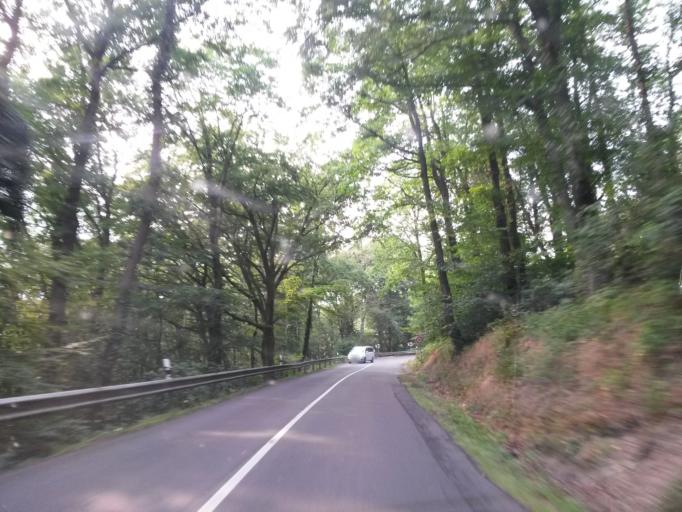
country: DE
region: North Rhine-Westphalia
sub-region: Regierungsbezirk Koln
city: Hennef
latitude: 50.7851
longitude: 7.2956
